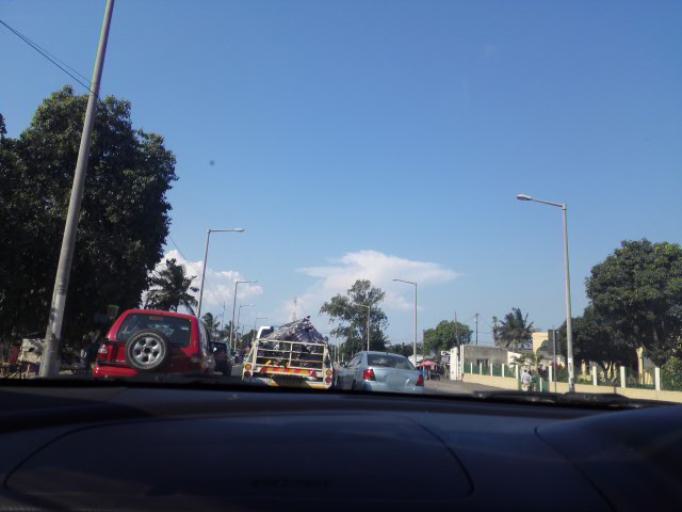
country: MZ
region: Maputo City
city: Maputo
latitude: -25.8842
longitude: 32.5666
